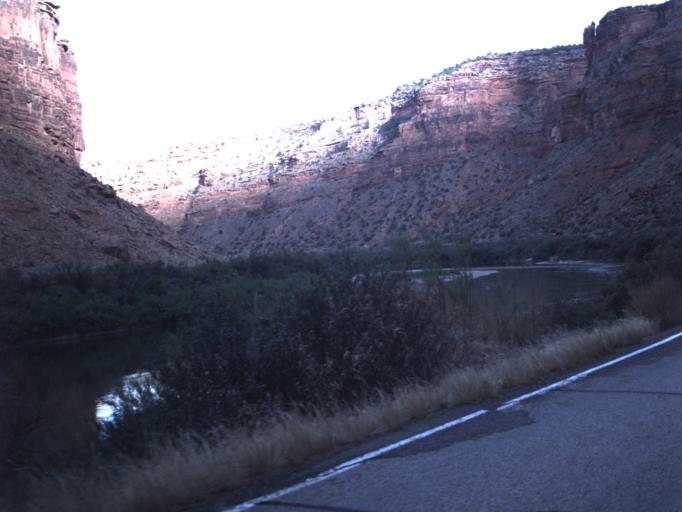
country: US
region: Utah
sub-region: Grand County
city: Moab
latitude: 38.7969
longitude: -109.3312
